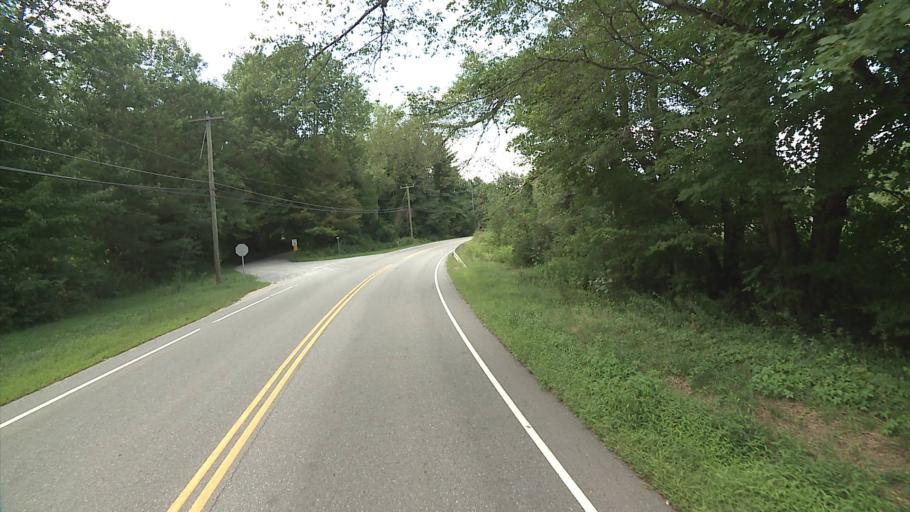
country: US
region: Connecticut
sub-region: New London County
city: Colchester
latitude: 41.6178
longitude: -72.2731
